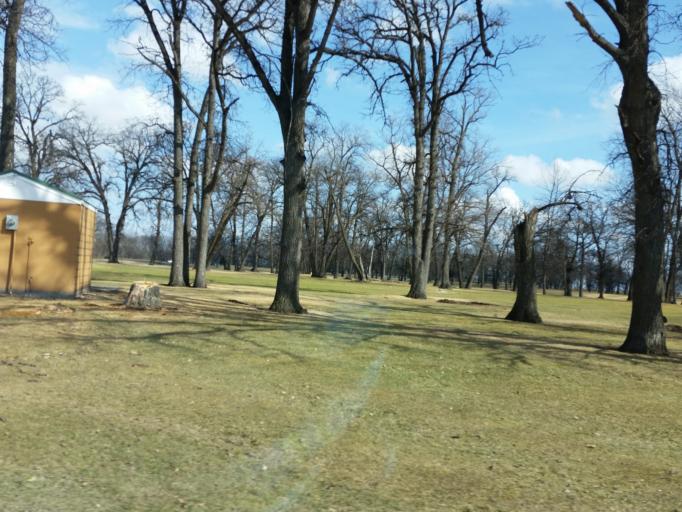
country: US
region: North Dakota
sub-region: Walsh County
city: Grafton
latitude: 48.4218
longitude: -97.3916
